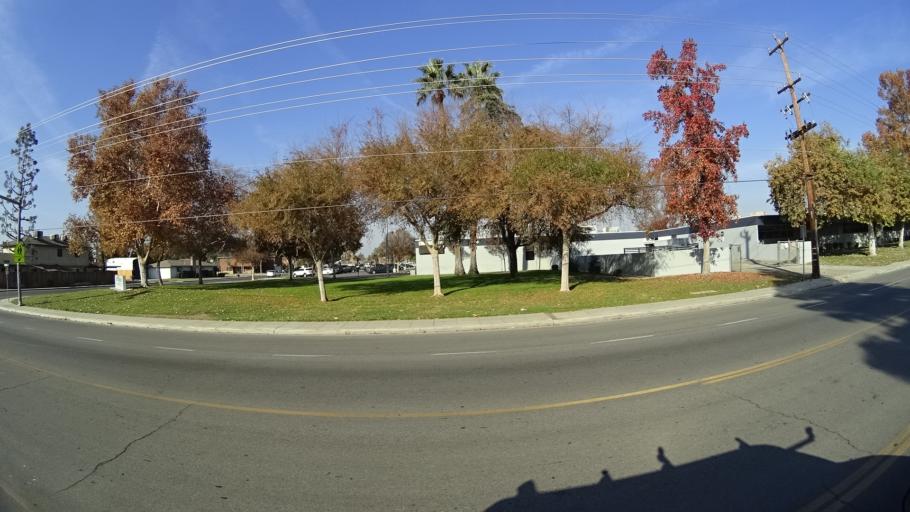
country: US
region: California
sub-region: Kern County
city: Bakersfield
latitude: 35.3249
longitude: -119.0519
